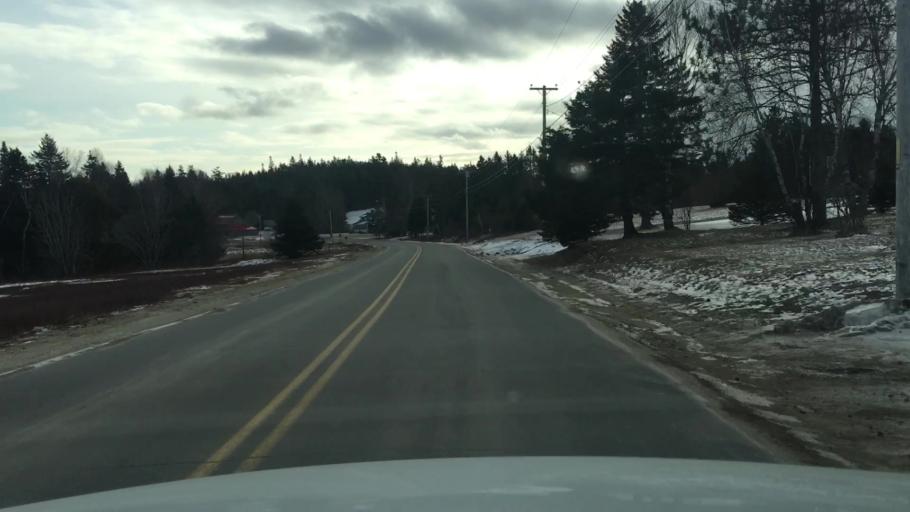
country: US
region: Maine
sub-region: Washington County
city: Jonesport
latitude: 44.6193
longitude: -67.6064
